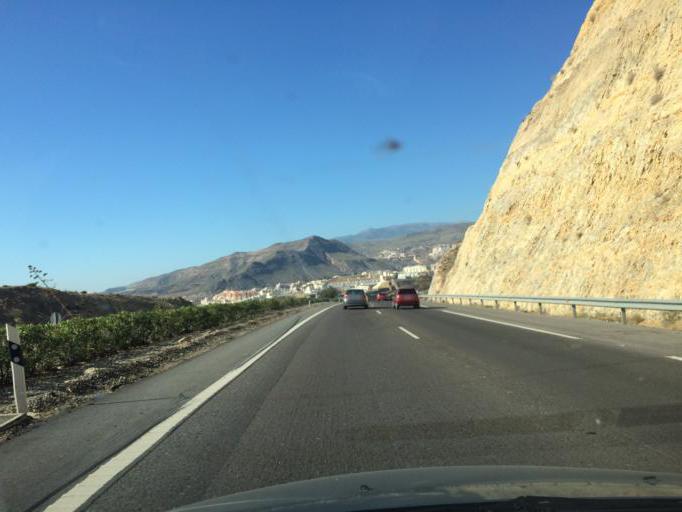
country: ES
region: Andalusia
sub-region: Provincia de Almeria
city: Aguadulce
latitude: 36.8219
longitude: -2.5711
